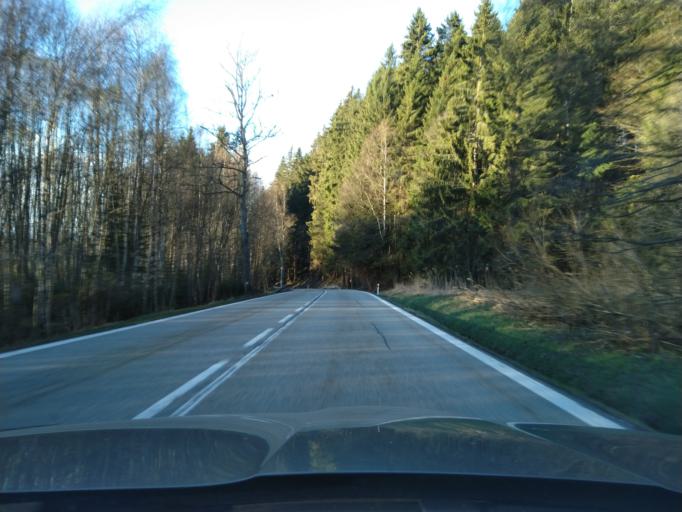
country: CZ
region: Jihocesky
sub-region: Okres Prachatice
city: Vimperk
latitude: 48.9731
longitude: 13.7617
